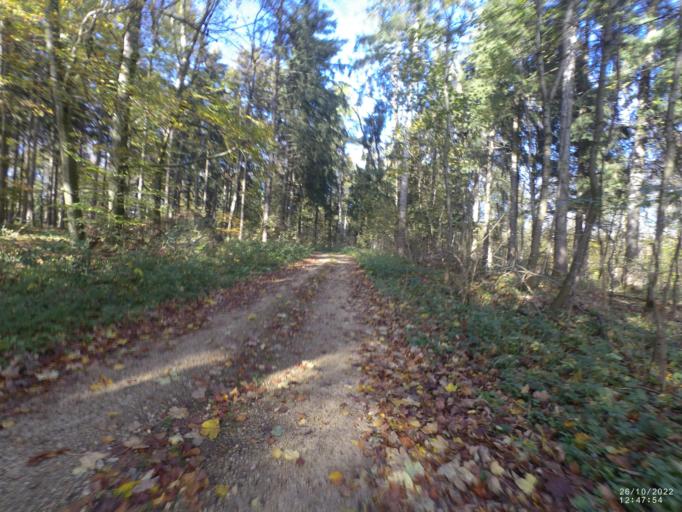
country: DE
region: Baden-Wuerttemberg
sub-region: Regierungsbezirk Stuttgart
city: Donzdorf
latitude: 48.6876
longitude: 9.8628
